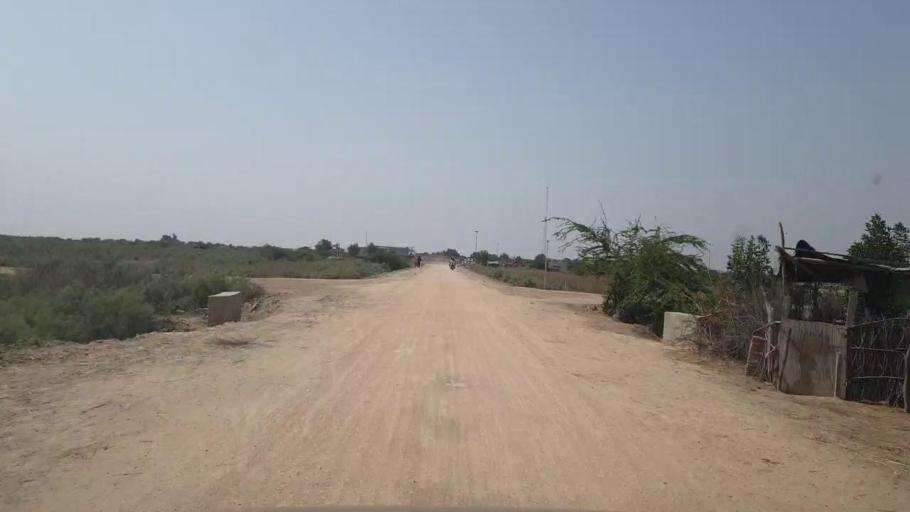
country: PK
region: Sindh
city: Jati
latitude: 24.3612
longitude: 68.5564
